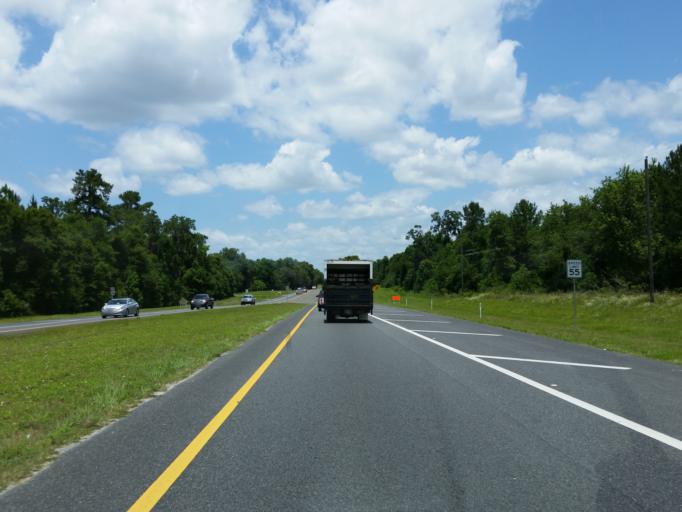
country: US
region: Florida
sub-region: Marion County
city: Belleview
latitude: 28.9839
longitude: -82.0412
